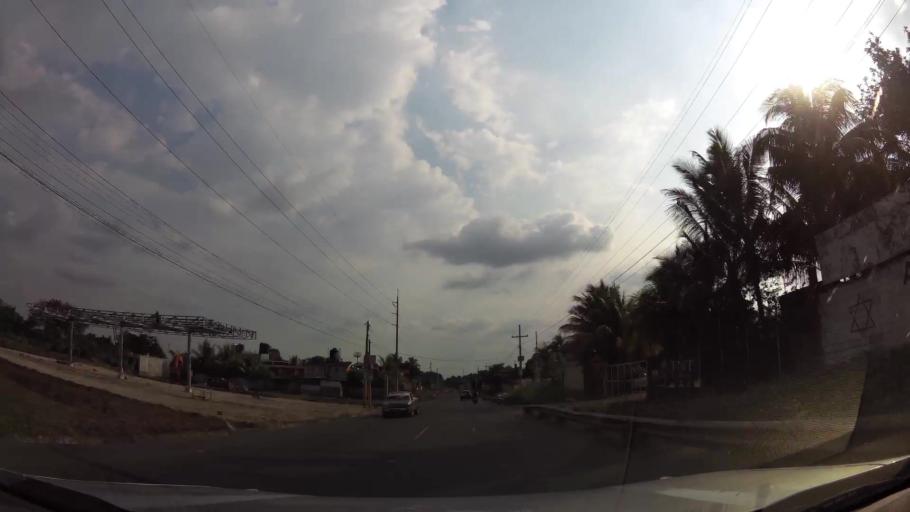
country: GT
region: Escuintla
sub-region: Municipio de Escuintla
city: Escuintla
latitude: 14.3146
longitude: -90.7932
